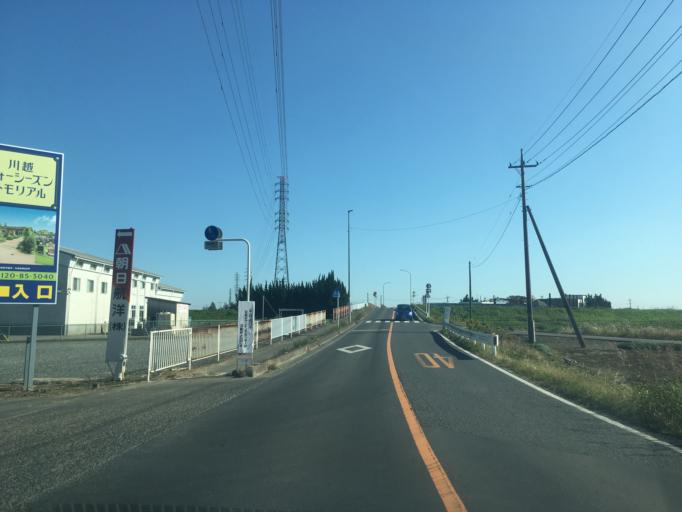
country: JP
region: Saitama
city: Kawagoe
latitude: 35.9487
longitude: 139.4585
